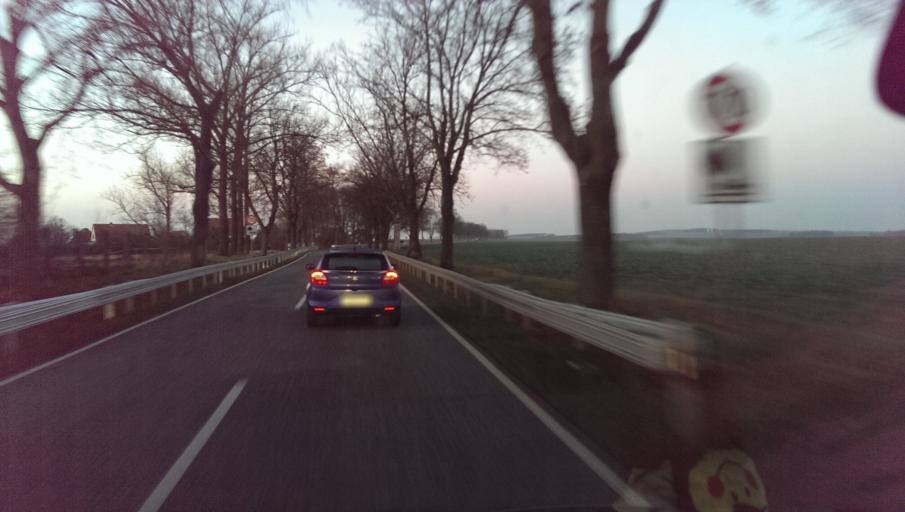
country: DE
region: Brandenburg
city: Juterbog
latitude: 51.9325
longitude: 13.1219
